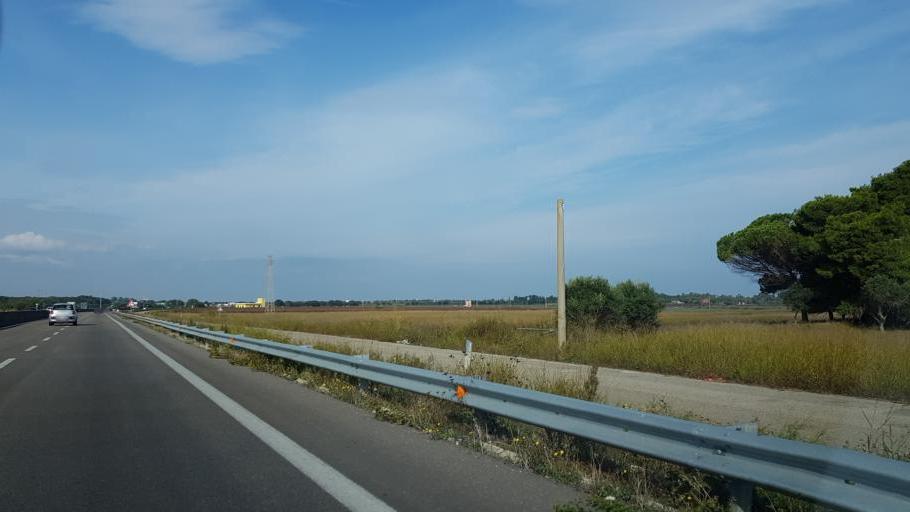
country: IT
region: Apulia
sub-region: Provincia di Brindisi
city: Brindisi
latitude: 40.6549
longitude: 17.9000
